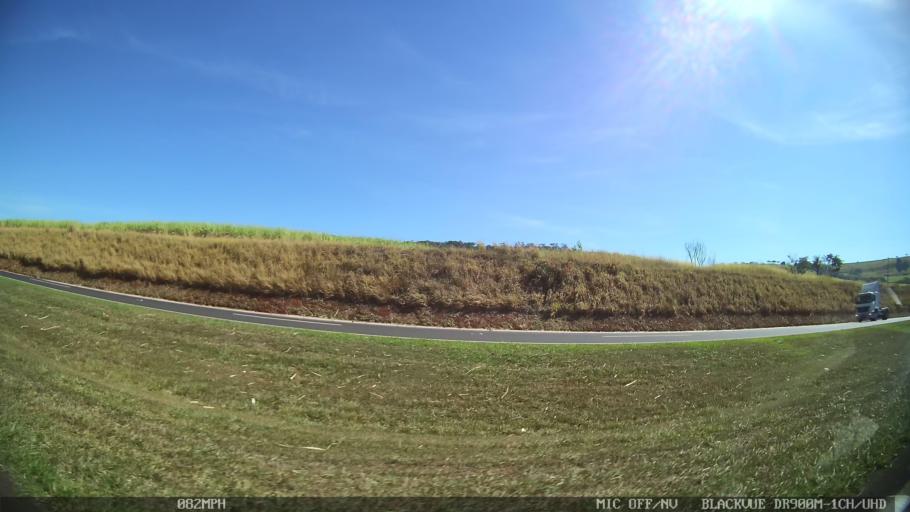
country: BR
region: Sao Paulo
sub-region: Sao Simao
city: Sao Simao
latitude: -21.4917
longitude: -47.6413
